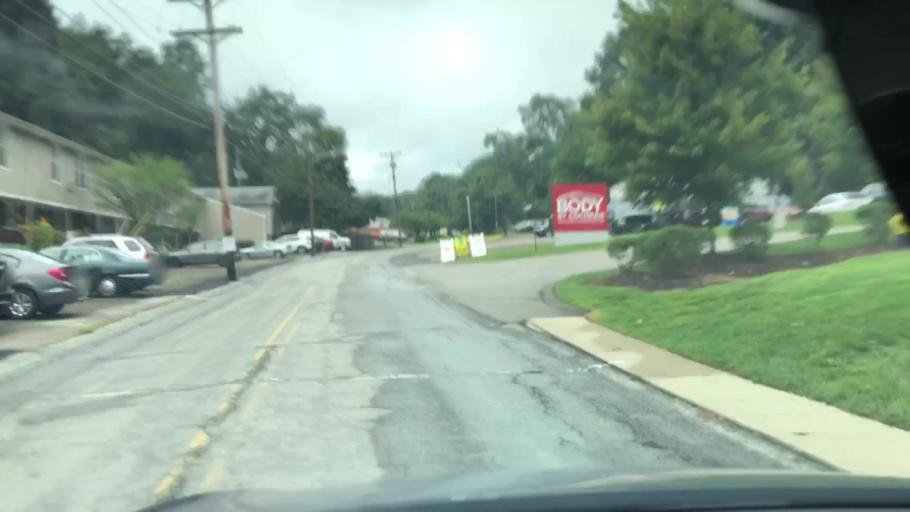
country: US
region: Pennsylvania
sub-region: Allegheny County
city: Castle Shannon
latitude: 40.3732
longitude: -80.0194
